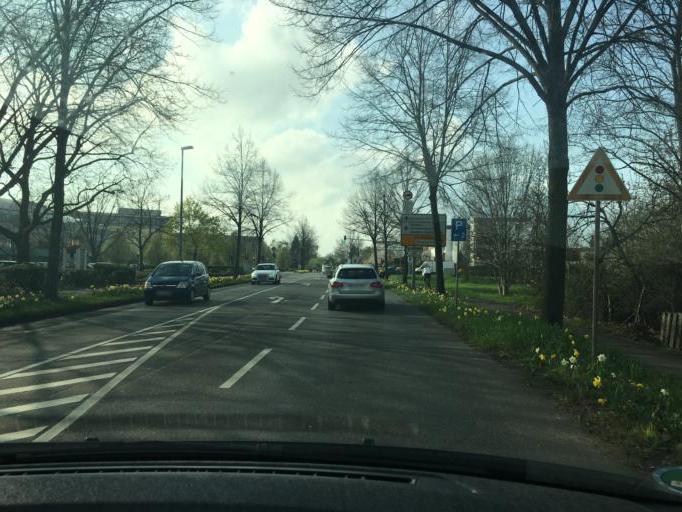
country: DE
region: North Rhine-Westphalia
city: Bornheim
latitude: 50.7580
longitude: 7.0056
